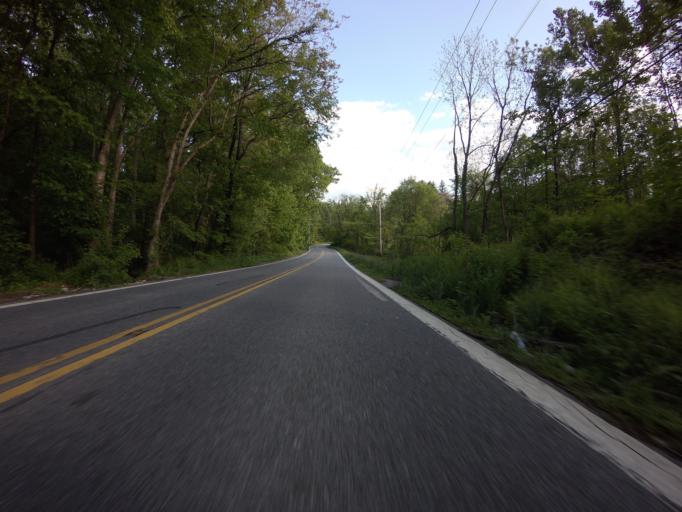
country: US
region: Maryland
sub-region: Baltimore County
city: Hunt Valley
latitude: 39.5040
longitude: -76.7115
